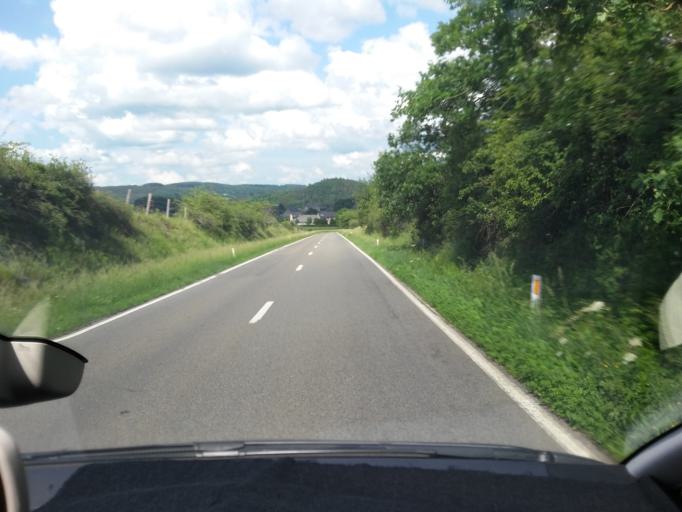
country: BE
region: Wallonia
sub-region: Province de Namur
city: Rochefort
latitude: 50.1251
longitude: 5.2613
